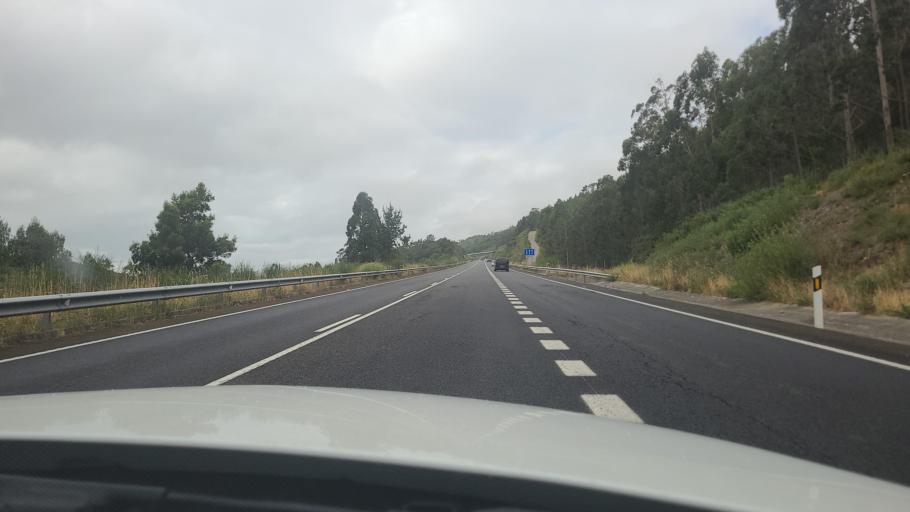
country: ES
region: Galicia
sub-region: Provincia da Coruna
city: Cee
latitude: 42.9716
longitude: -9.1985
